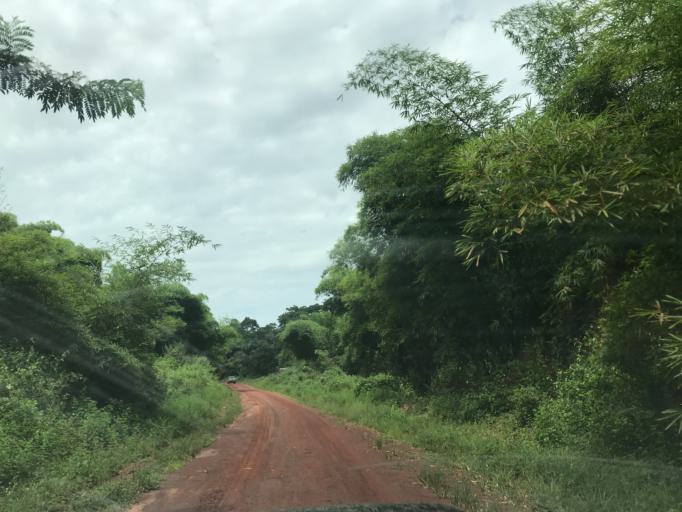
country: CD
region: Eastern Province
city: Buta
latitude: 2.3462
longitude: 24.9557
